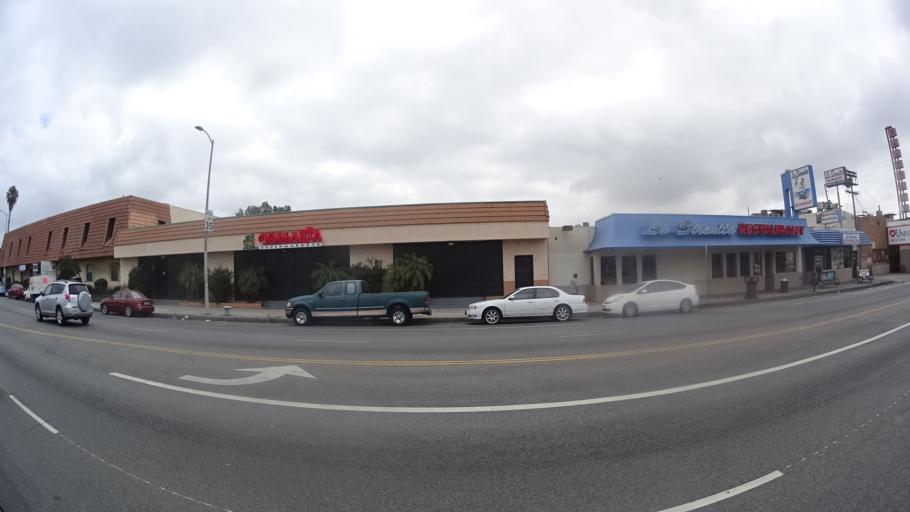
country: US
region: California
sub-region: Los Angeles County
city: San Fernando
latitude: 34.2361
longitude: -118.4504
